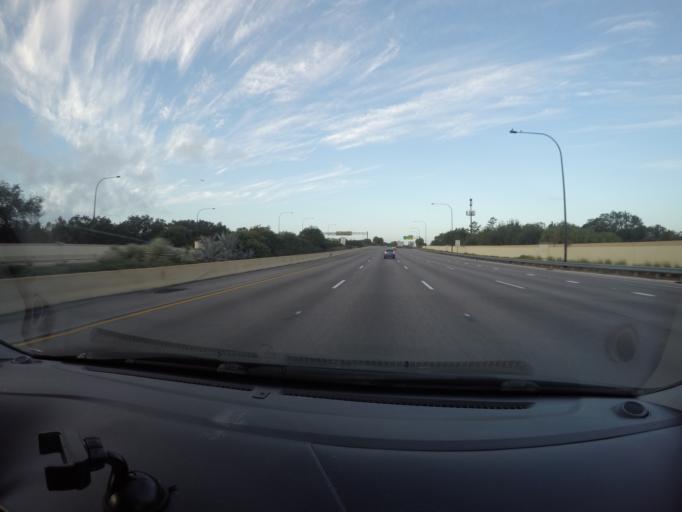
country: US
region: Florida
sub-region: Orange County
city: Orlando
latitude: 28.5379
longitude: -81.3616
